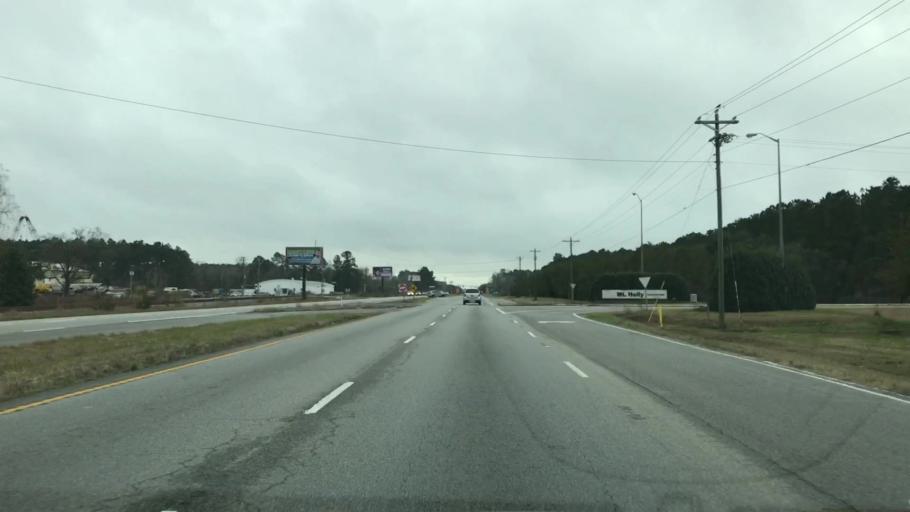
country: US
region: South Carolina
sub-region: Berkeley County
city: Goose Creek
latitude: 33.0392
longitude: -80.0337
